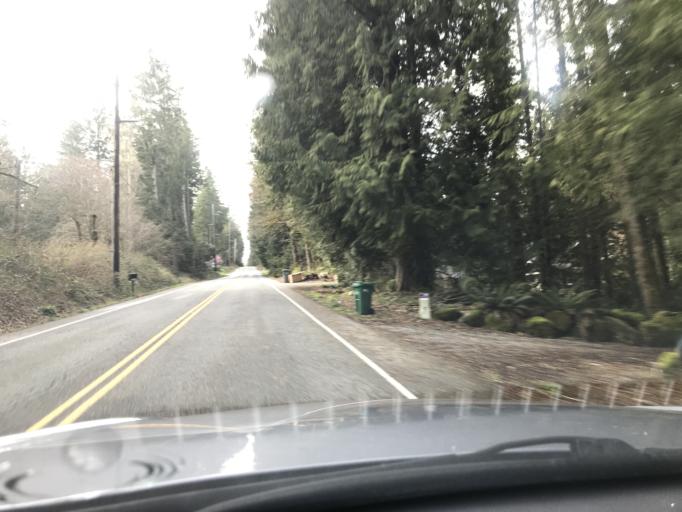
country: US
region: Washington
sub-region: King County
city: Ames Lake
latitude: 47.6504
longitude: -121.9743
